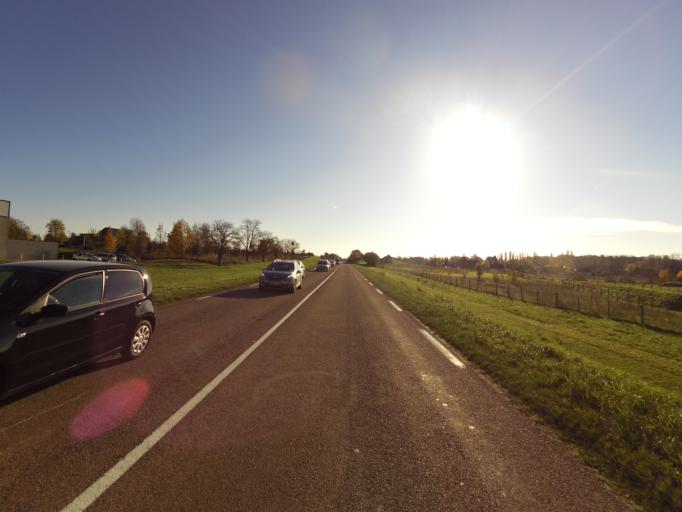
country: FR
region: Champagne-Ardenne
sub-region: Departement de l'Aube
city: Rosieres-pres-Troyes
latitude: 48.2657
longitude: 4.0742
